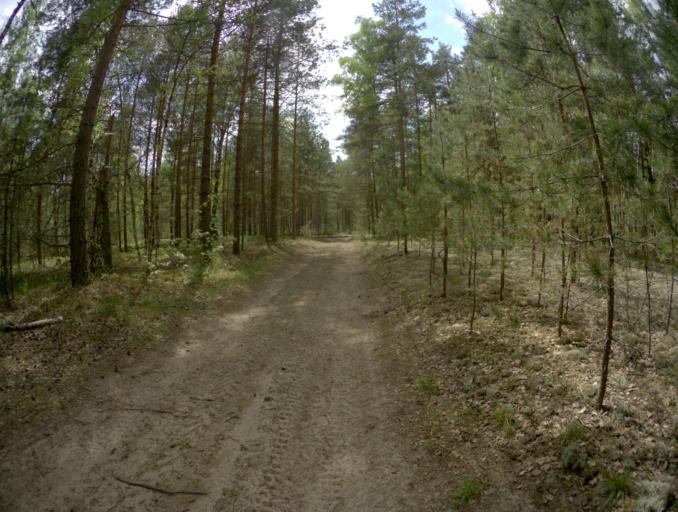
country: RU
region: Vladimir
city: Ivanishchi
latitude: 55.6930
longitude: 40.4251
